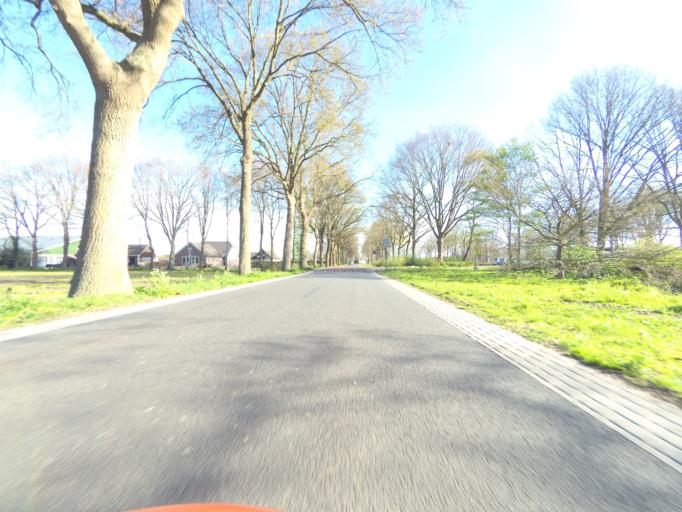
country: NL
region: Gelderland
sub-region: Gemeente Putten
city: Putten
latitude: 52.2506
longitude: 5.5915
